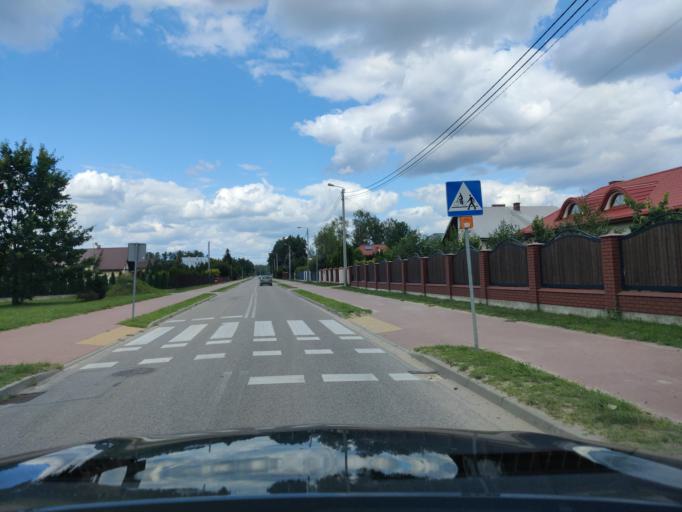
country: PL
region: Masovian Voivodeship
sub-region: Powiat wegrowski
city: Wegrow
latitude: 52.4076
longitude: 22.0299
